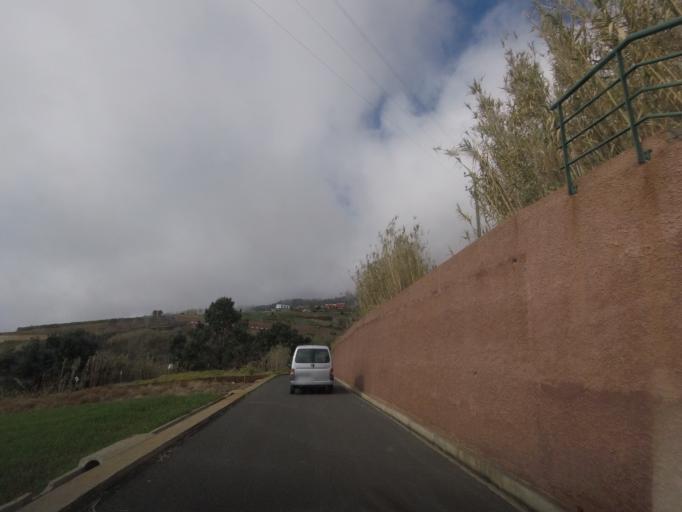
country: PT
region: Madeira
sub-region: Calheta
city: Faja da Ovelha
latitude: 32.7646
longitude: -17.2205
